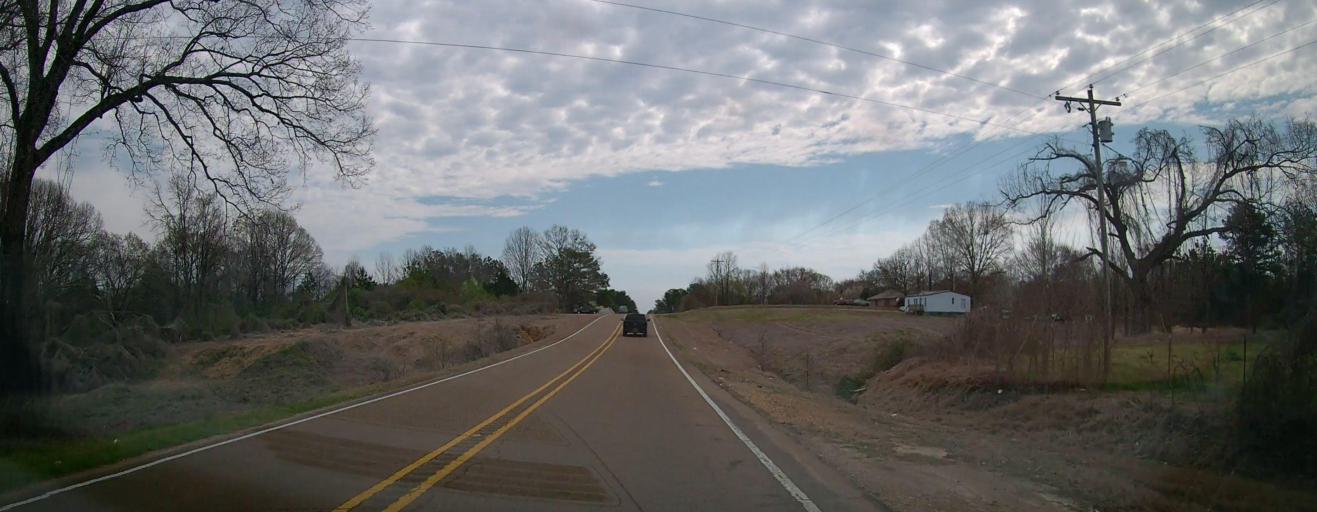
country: US
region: Mississippi
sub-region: Marshall County
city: Byhalia
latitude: 34.8429
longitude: -89.6080
